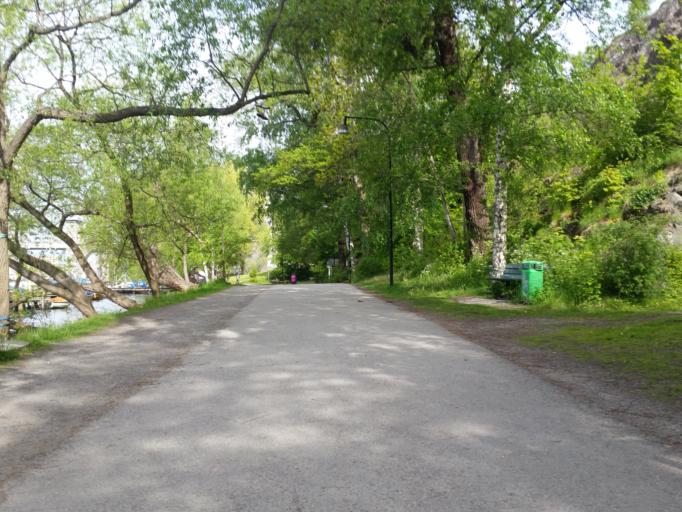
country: SE
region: Stockholm
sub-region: Stockholms Kommun
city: Arsta
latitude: 59.3080
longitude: 18.0522
